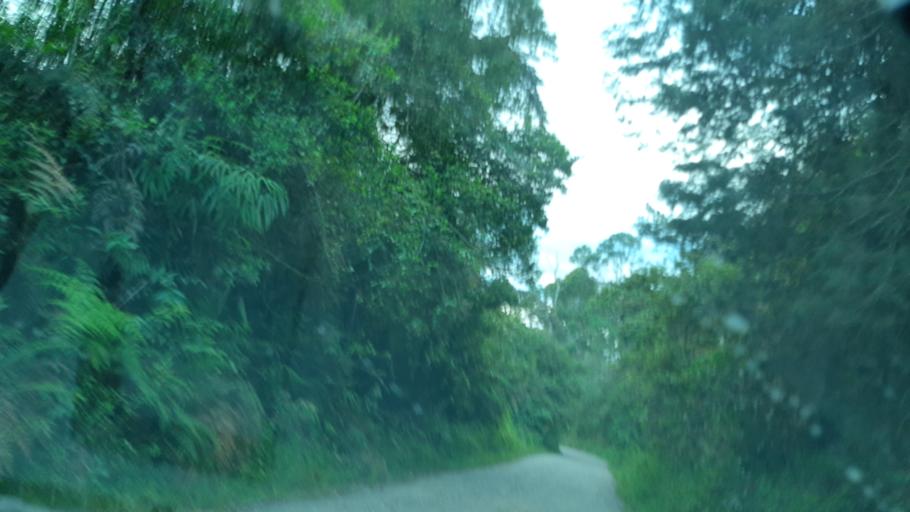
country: CO
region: Boyaca
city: Garagoa
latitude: 5.0853
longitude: -73.3254
